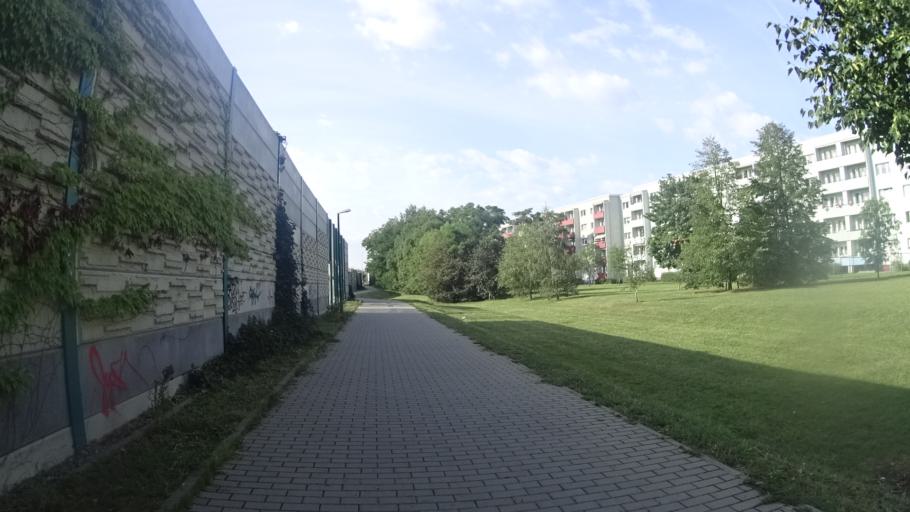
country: DE
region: Brandenburg
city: Brandenburg an der Havel
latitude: 52.4273
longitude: 12.5307
